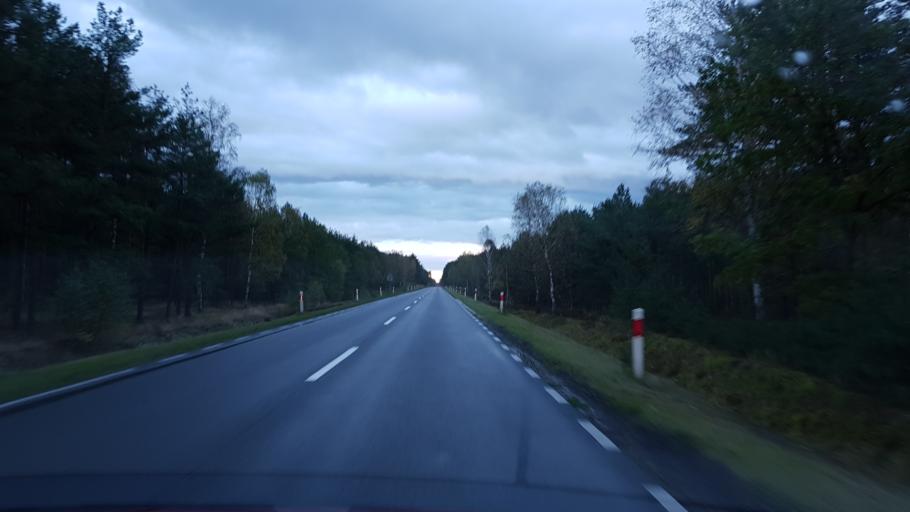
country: PL
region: Greater Poland Voivodeship
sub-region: Powiat pilski
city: Smilowo
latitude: 53.2022
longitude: 16.8389
